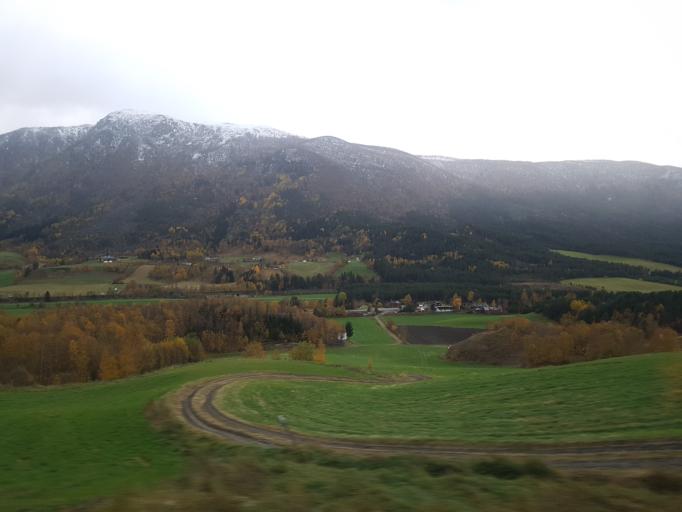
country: NO
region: Oppland
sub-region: Dovre
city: Dovre
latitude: 62.0011
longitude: 9.2225
